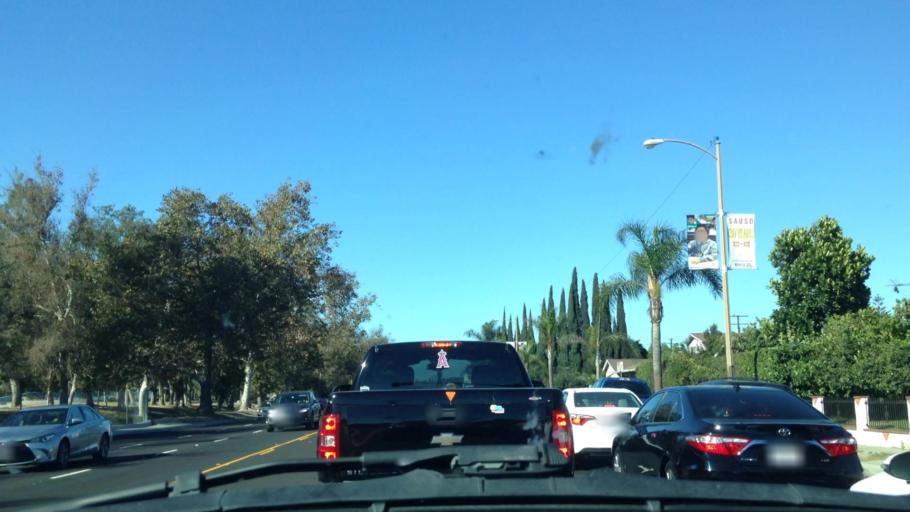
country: US
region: California
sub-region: Orange County
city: Santa Ana
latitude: 33.7238
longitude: -117.9074
